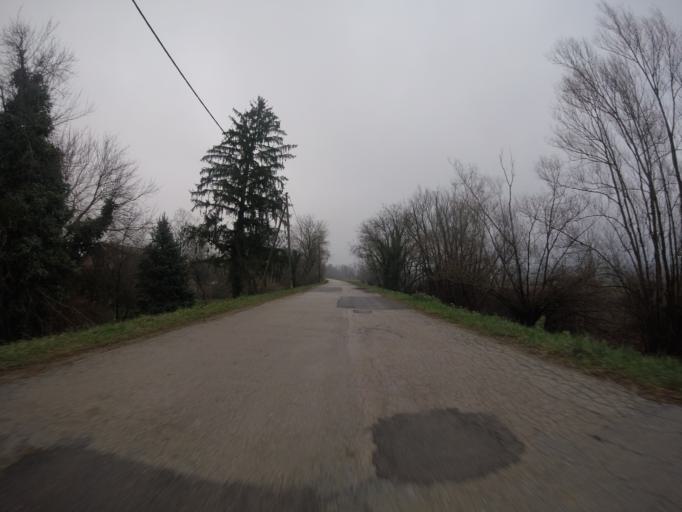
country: HR
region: Zagrebacka
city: Kuce
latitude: 45.7094
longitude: 16.2189
